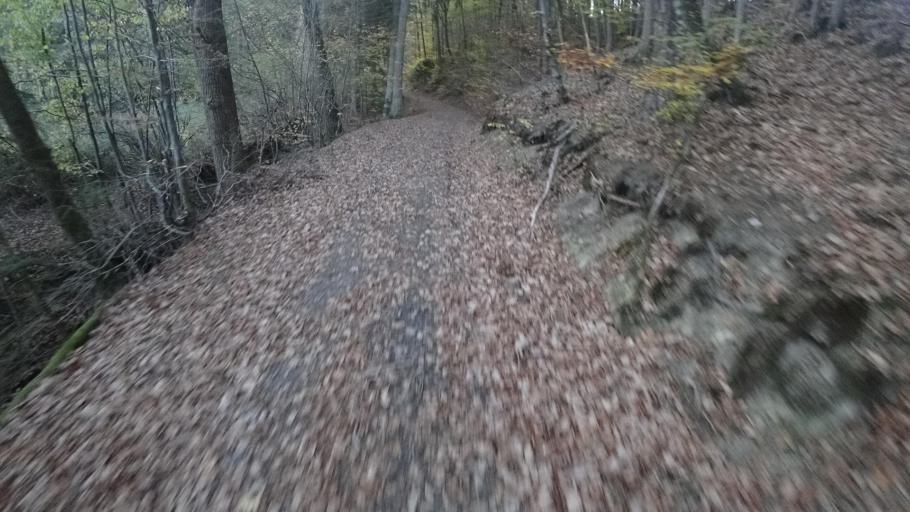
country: DE
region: Rheinland-Pfalz
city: Berg
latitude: 50.5350
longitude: 6.9538
